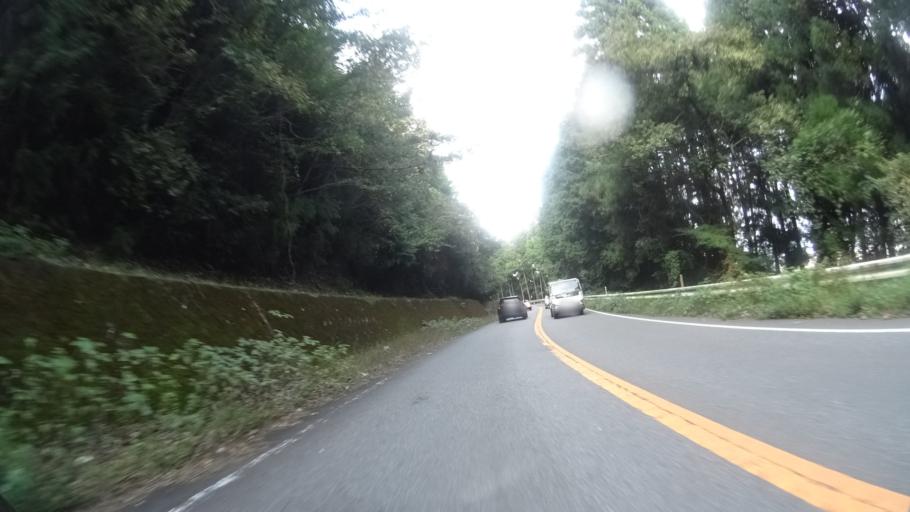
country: JP
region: Oita
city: Beppu
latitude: 33.2865
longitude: 131.4579
